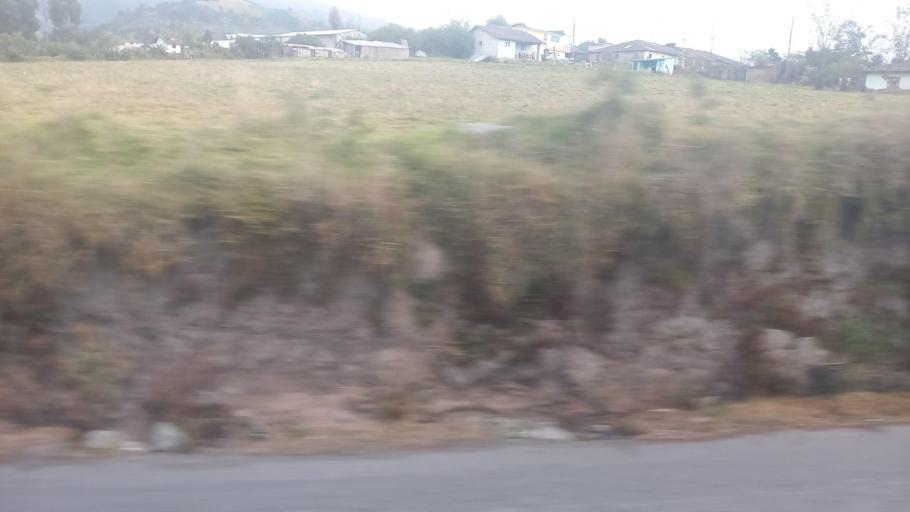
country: EC
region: Pichincha
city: Cayambe
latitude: 0.0727
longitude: -78.1097
